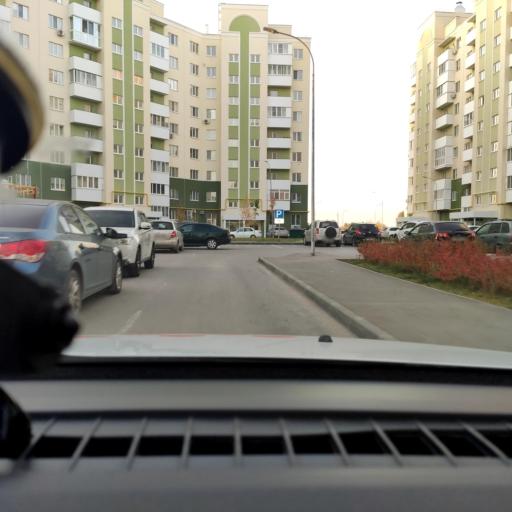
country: RU
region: Samara
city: Samara
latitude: 53.1087
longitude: 50.1390
